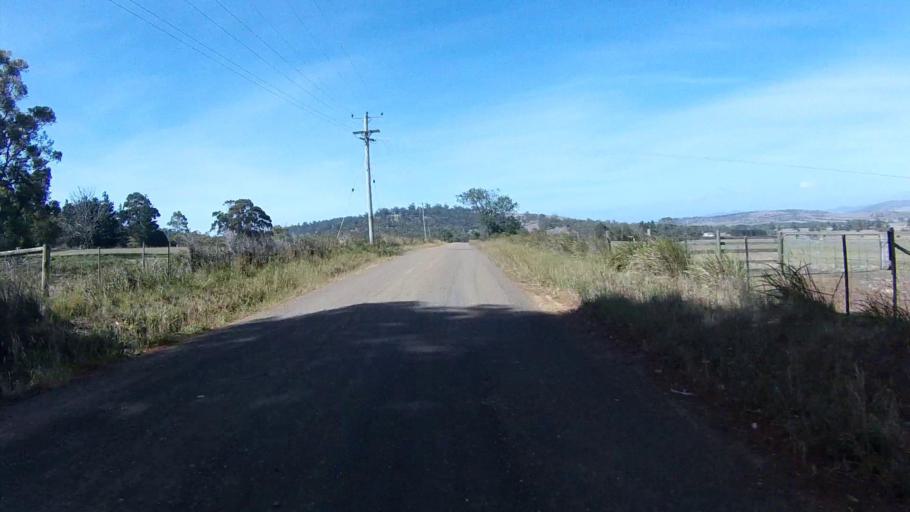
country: AU
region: Tasmania
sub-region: Sorell
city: Sorell
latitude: -42.7268
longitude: 147.5967
